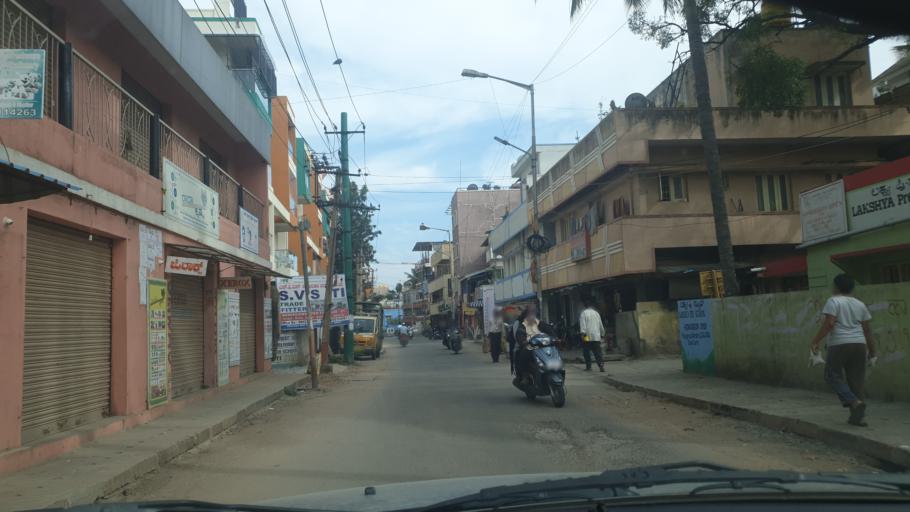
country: IN
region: Karnataka
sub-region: Bangalore Urban
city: Bangalore
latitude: 12.9649
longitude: 77.6792
